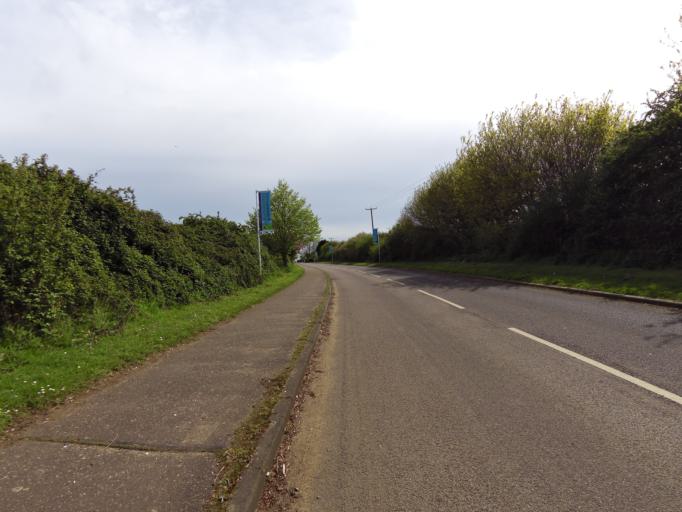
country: GB
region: England
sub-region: Essex
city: Mistley
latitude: 51.9731
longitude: 1.1373
